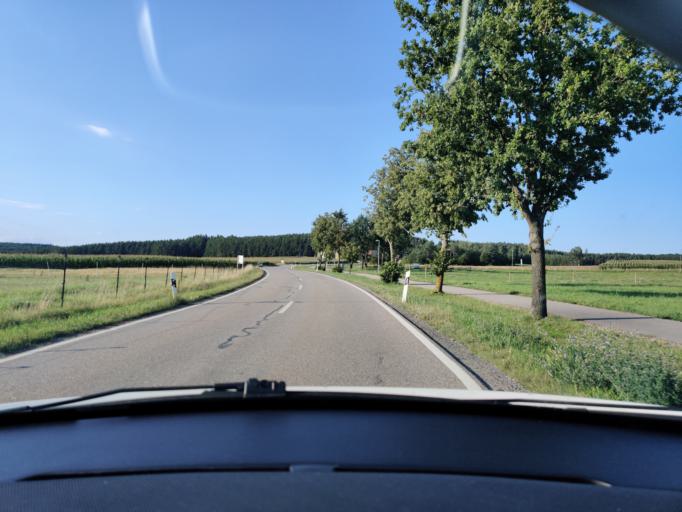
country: DE
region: Bavaria
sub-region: Upper Palatinate
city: Stulln
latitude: 49.4234
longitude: 12.1385
